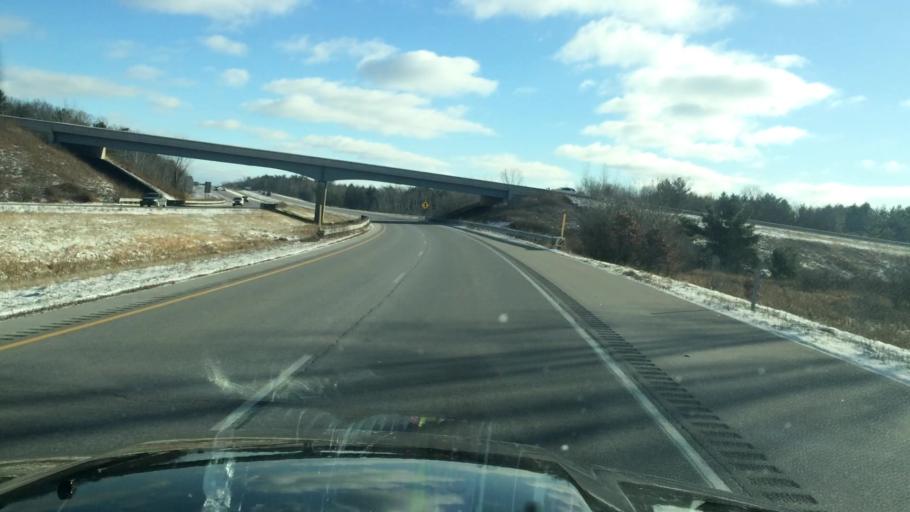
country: US
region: Wisconsin
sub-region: Portage County
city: Stevens Point
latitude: 44.5486
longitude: -89.5782
